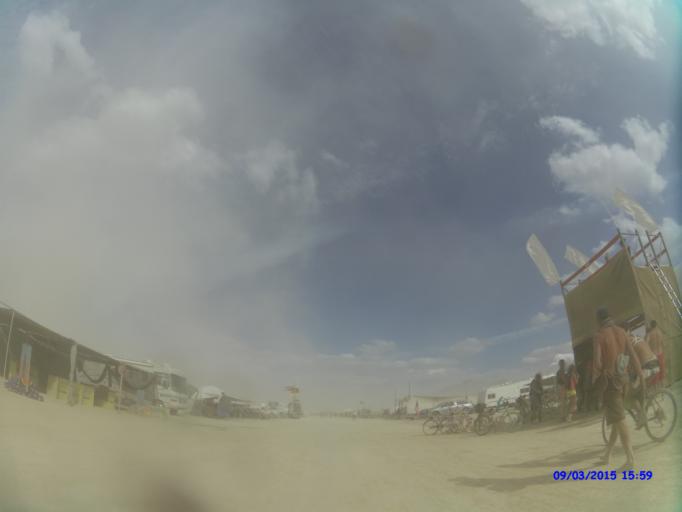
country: US
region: Nevada
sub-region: Pershing County
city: Lovelock
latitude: 40.7772
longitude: -119.2092
